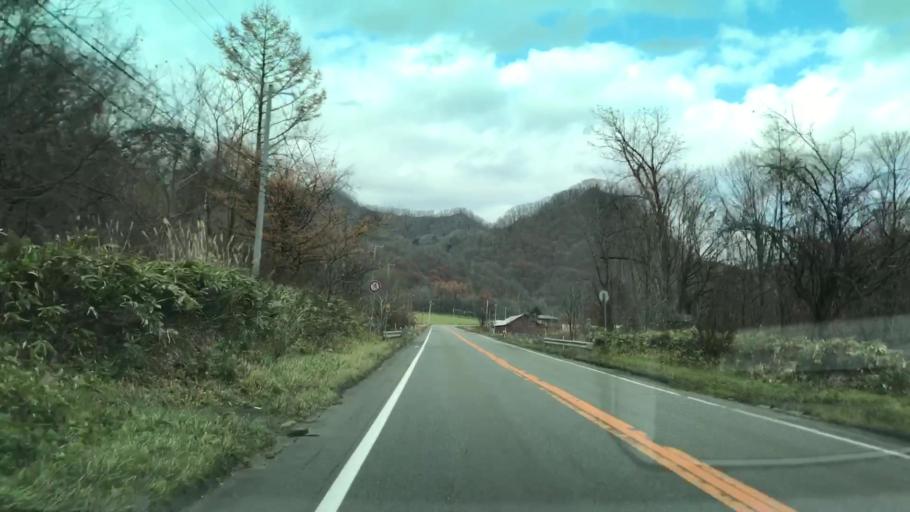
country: JP
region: Hokkaido
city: Shizunai-furukawacho
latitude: 42.8012
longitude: 142.3978
